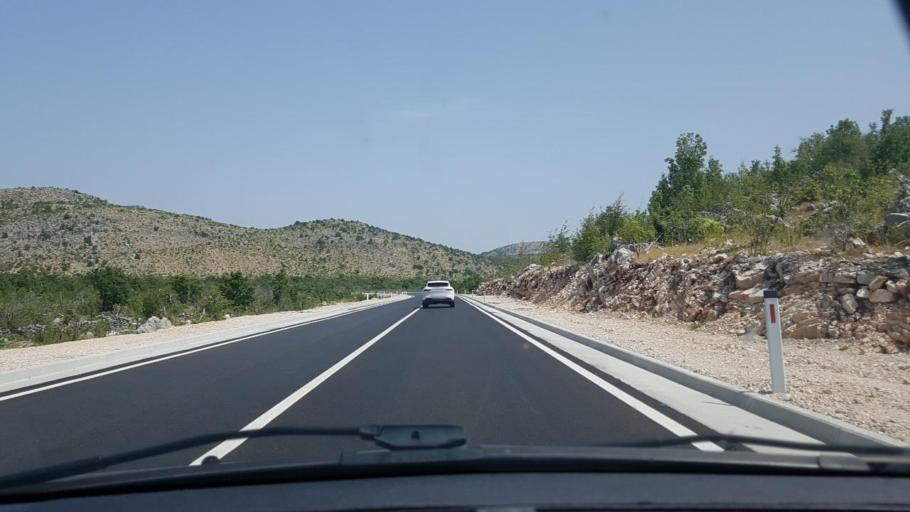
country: HR
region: Dubrovacko-Neretvanska
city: Podgora
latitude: 42.9455
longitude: 17.7701
